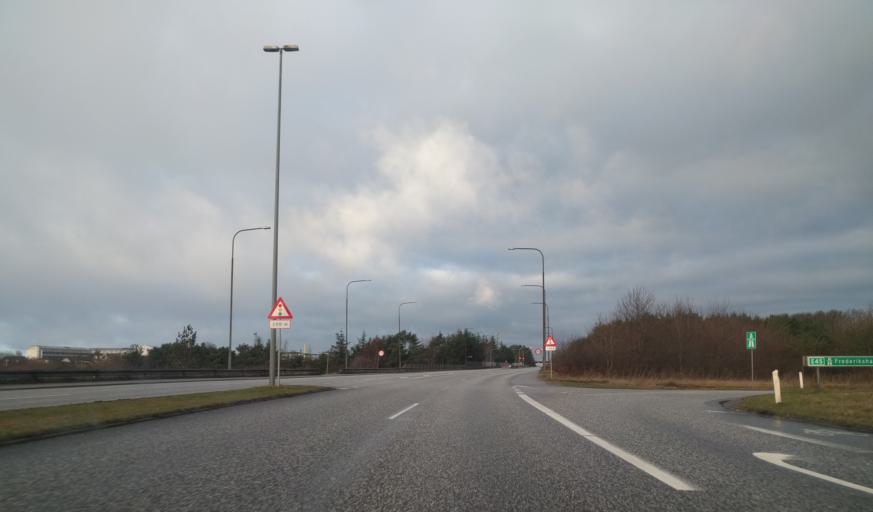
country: DK
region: North Denmark
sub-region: Alborg Kommune
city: Gistrup
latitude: 57.0306
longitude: 9.9746
